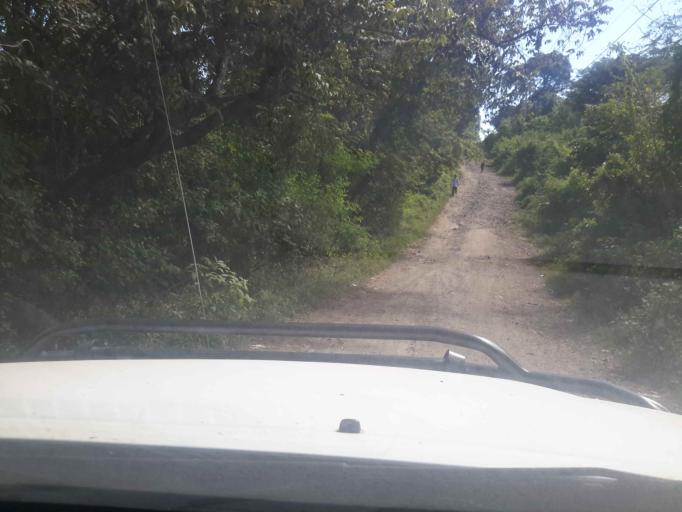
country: NI
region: Rivas
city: Altagracia
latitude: 11.4714
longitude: -85.4646
